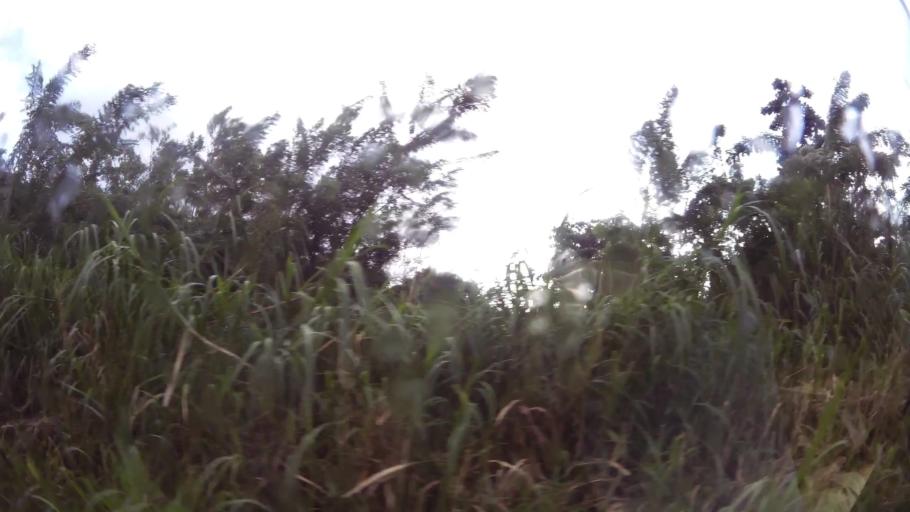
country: DM
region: Saint George
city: Roseau
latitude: 15.3237
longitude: -61.3902
